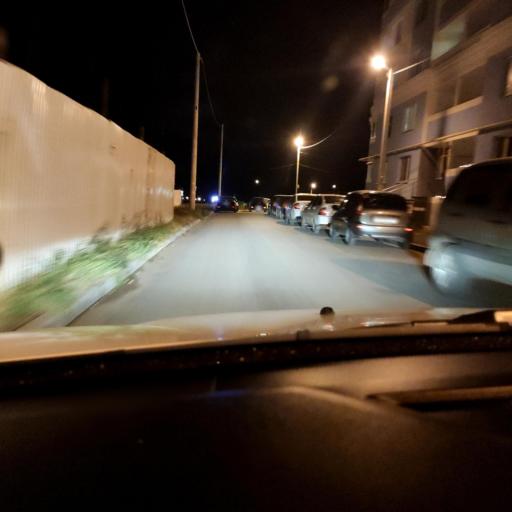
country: RU
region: Samara
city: Volzhskiy
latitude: 53.4355
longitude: 50.1233
